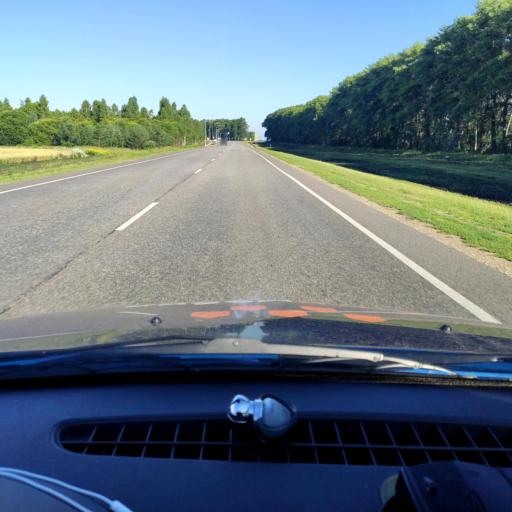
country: RU
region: Orjol
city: Pokrovskoye
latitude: 52.6396
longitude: 36.6766
